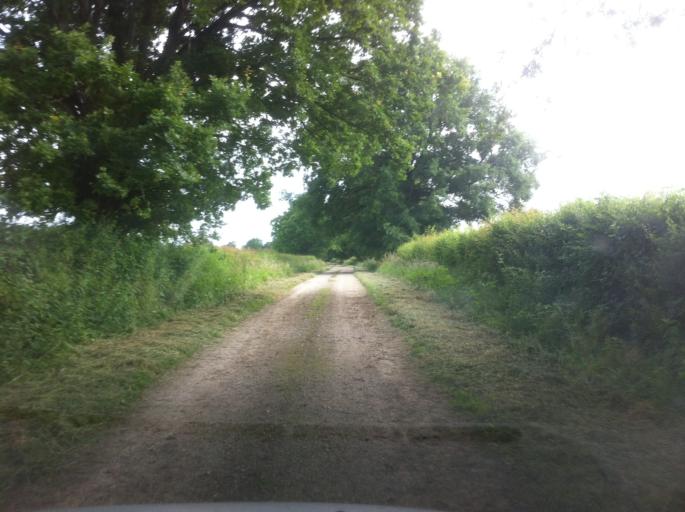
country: FR
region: Auvergne
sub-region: Departement de l'Allier
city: Chantelle
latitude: 46.3227
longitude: 3.1070
